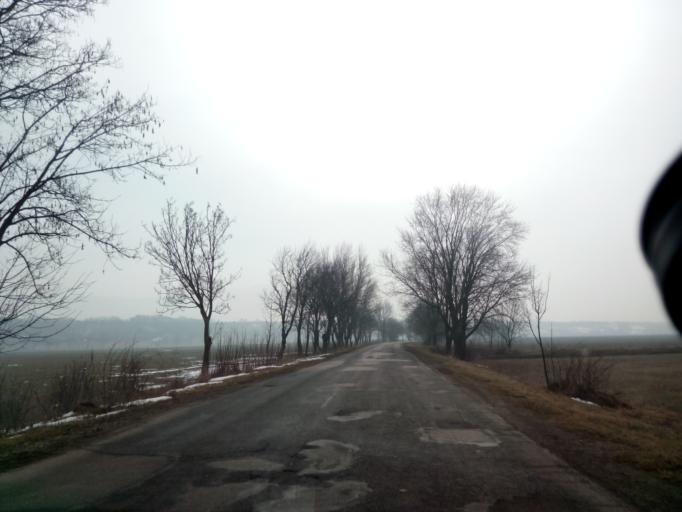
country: HU
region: Borsod-Abauj-Zemplen
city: Gonc
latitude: 48.4910
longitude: 21.2499
